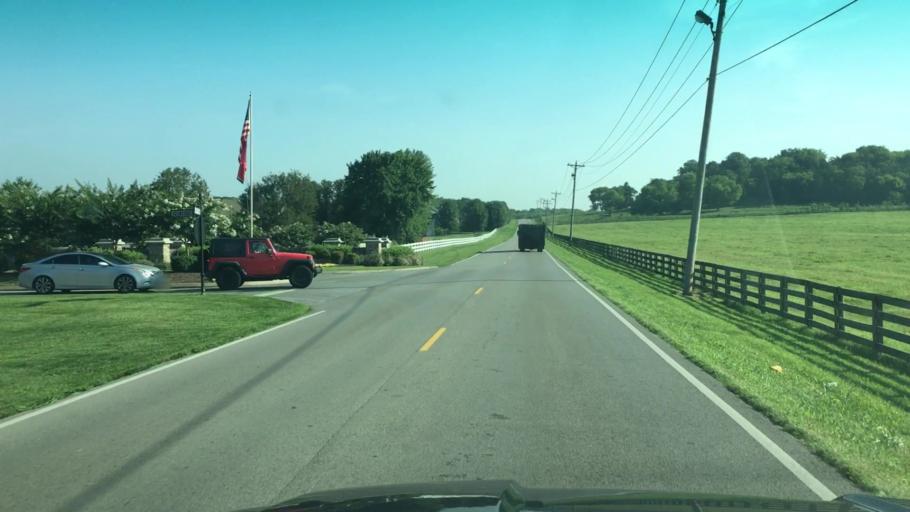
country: US
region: Tennessee
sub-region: Williamson County
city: Thompson's Station
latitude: 35.7848
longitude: -86.8784
